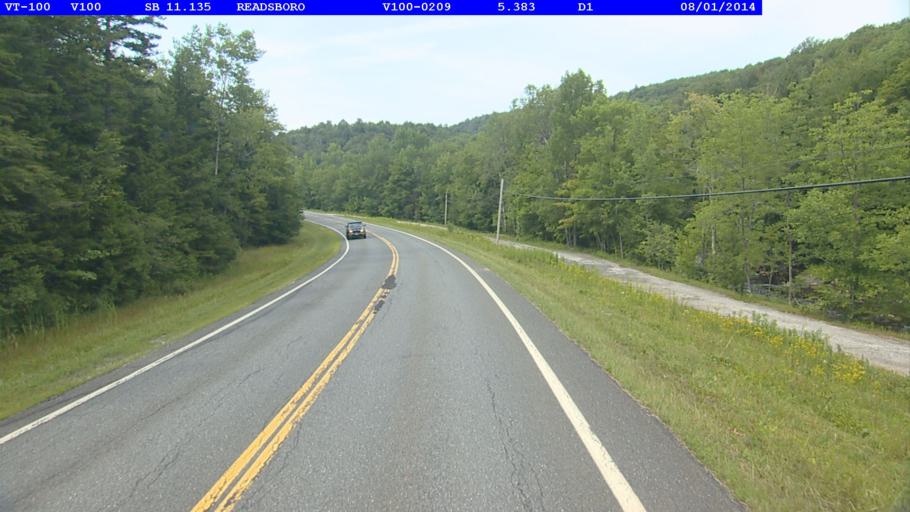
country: US
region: Massachusetts
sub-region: Berkshire County
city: North Adams
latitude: 42.7897
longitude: -72.9615
